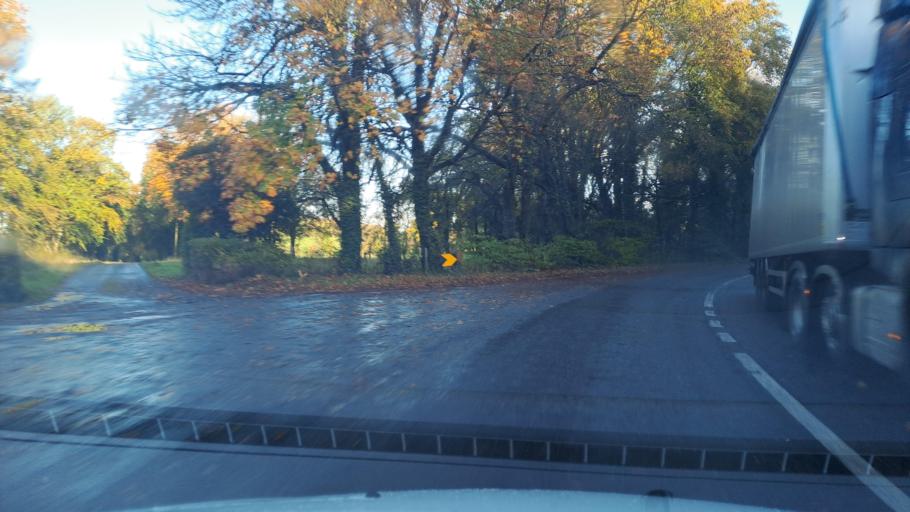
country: IE
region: Ulster
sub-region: An Cabhan
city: Cootehill
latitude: 54.0886
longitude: -7.0888
